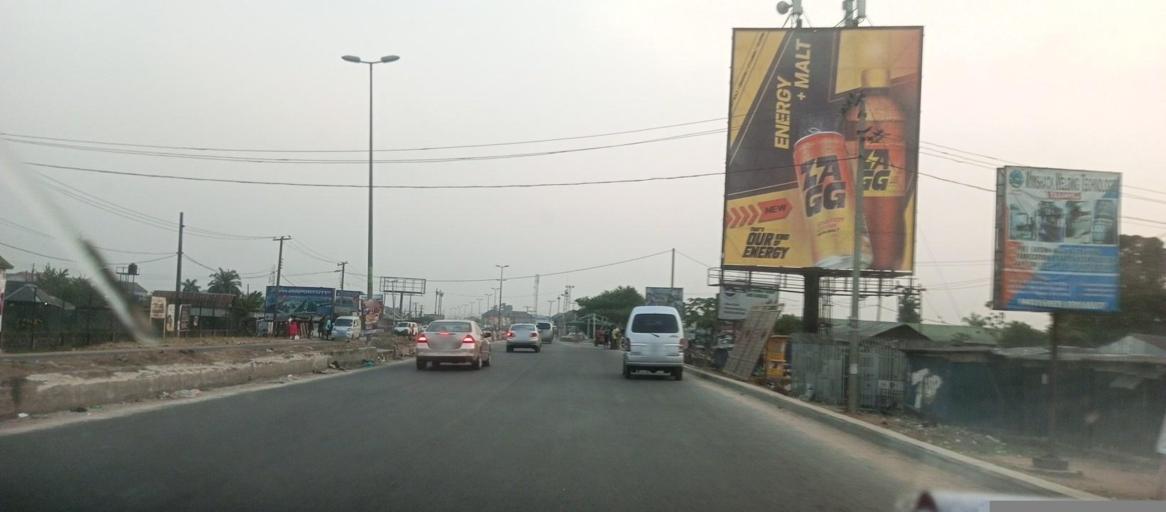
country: NG
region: Rivers
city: Emuoha
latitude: 4.9204
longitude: 6.9971
